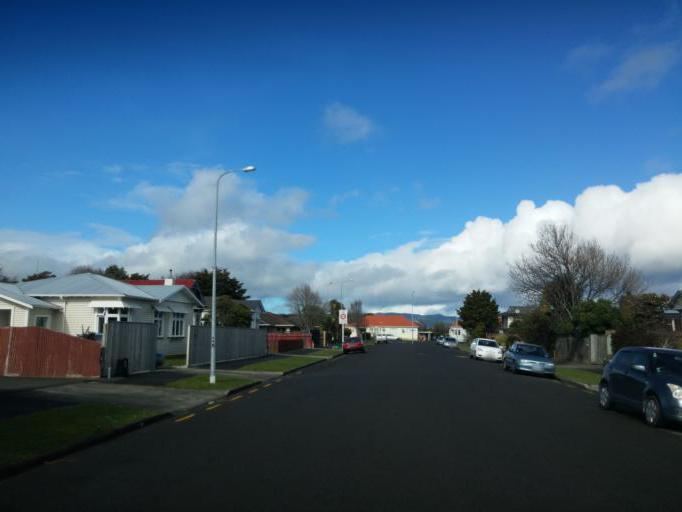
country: NZ
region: Manawatu-Wanganui
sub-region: Palmerston North City
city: Palmerston North
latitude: -40.3591
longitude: 175.6199
